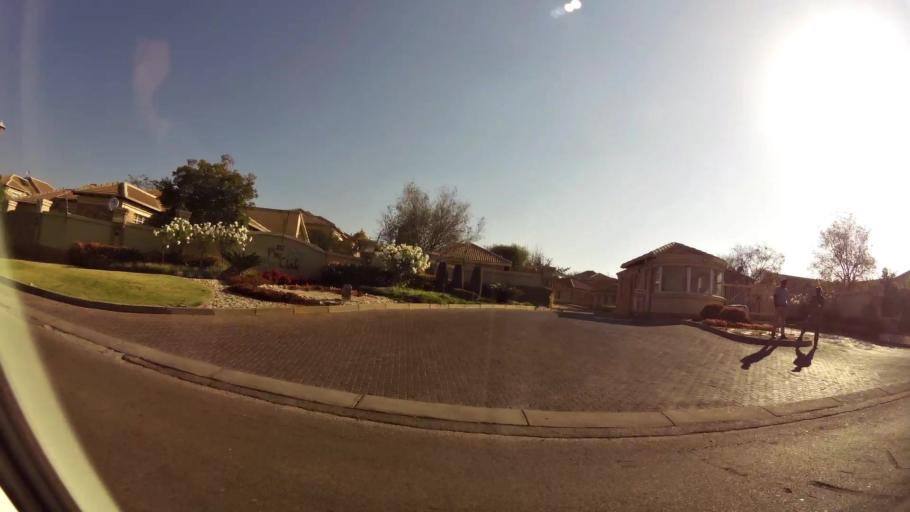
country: ZA
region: Gauteng
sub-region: City of Tshwane Metropolitan Municipality
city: Centurion
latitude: -25.8390
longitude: 28.2958
